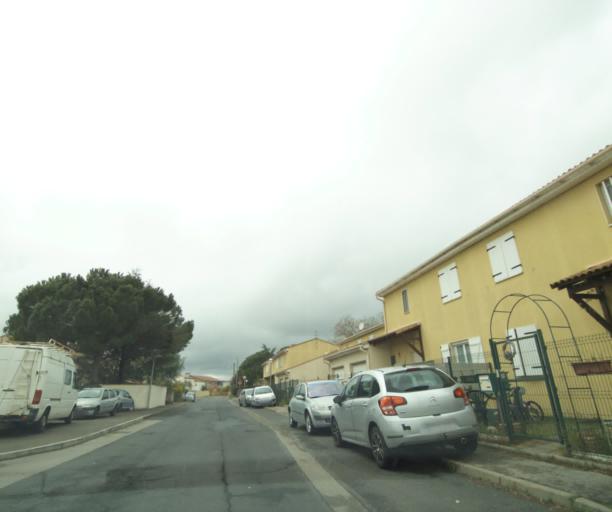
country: FR
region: Languedoc-Roussillon
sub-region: Departement de l'Herault
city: Cournonterral
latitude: 43.5575
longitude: 3.7278
